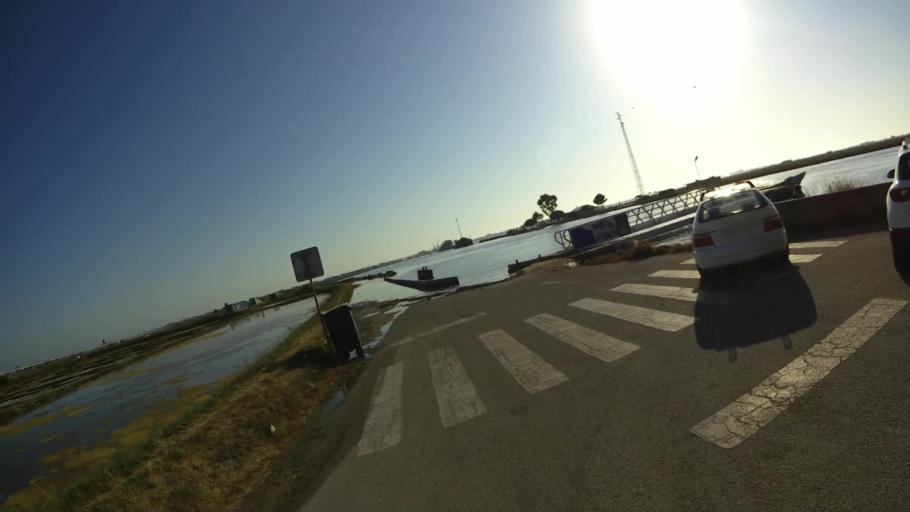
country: PT
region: Aveiro
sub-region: Aveiro
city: Aveiro
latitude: 40.6457
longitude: -8.6630
